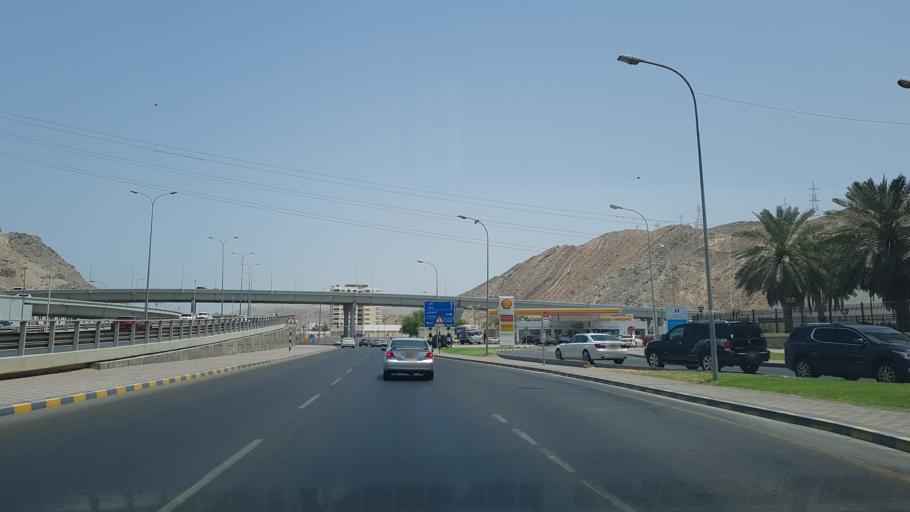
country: OM
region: Muhafazat Masqat
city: Muscat
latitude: 23.5924
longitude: 58.5241
